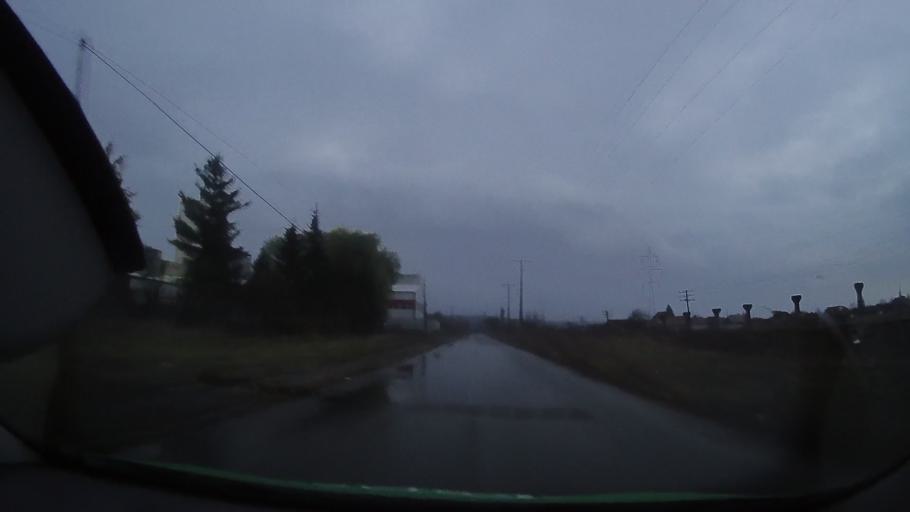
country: RO
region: Mures
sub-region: Municipiul Reghin
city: Iernuteni
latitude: 46.7695
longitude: 24.7222
